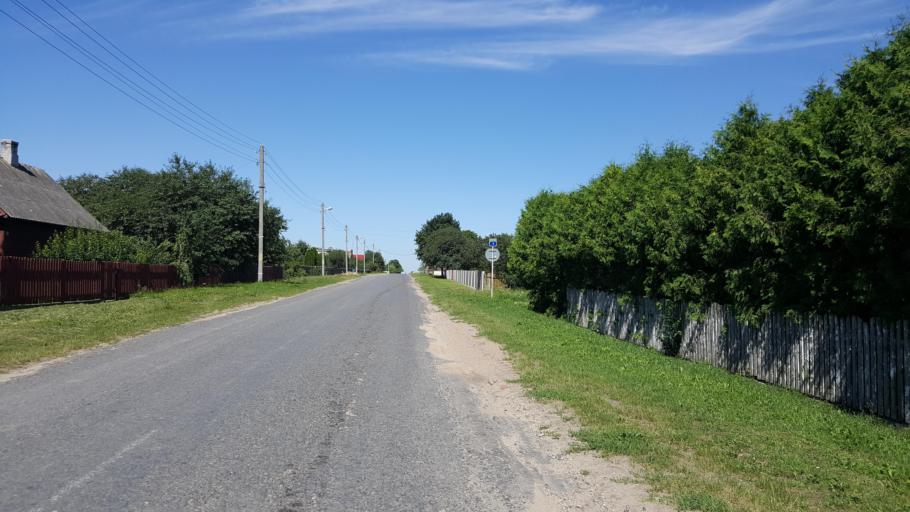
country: BY
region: Brest
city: Charnawchytsy
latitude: 52.2252
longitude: 23.7378
